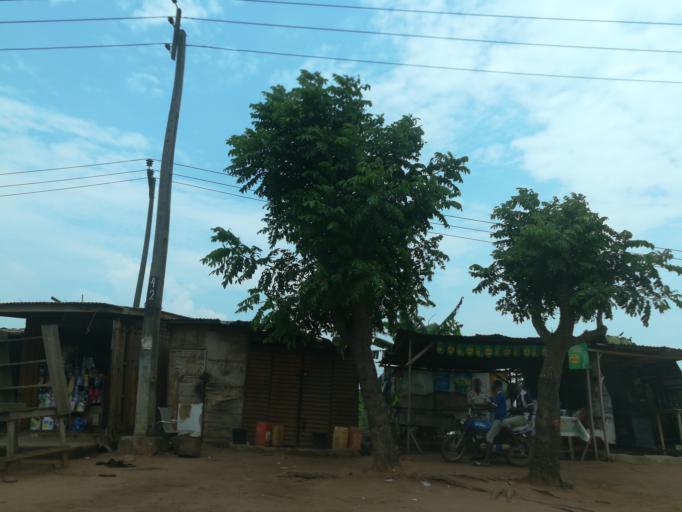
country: NG
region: Lagos
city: Ikorodu
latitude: 6.5804
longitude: 3.5894
